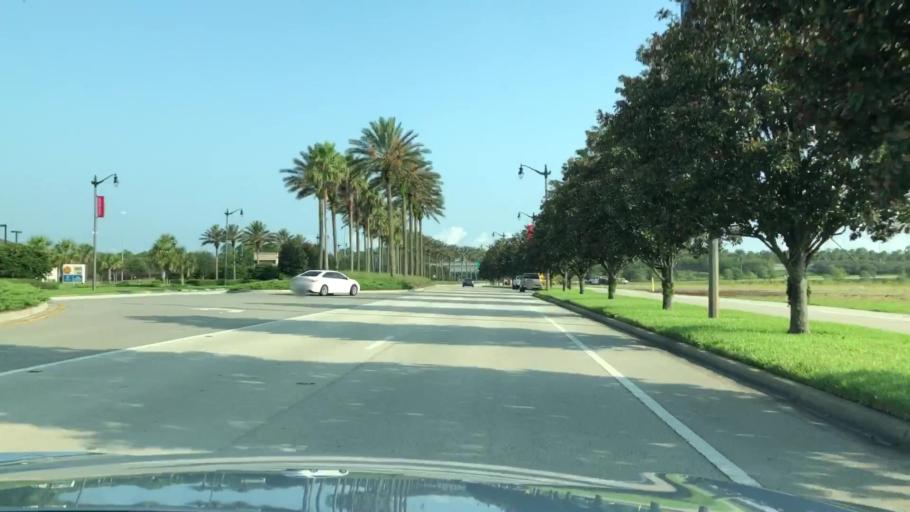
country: US
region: Florida
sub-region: Saint Johns County
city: Palm Valley
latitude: 30.1104
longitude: -81.4166
